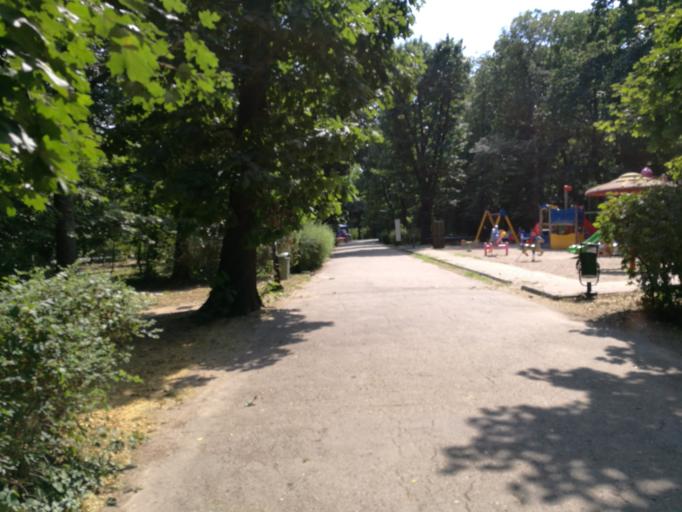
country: RO
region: Bucuresti
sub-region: Municipiul Bucuresti
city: Bucuresti
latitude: 44.4704
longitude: 26.0809
